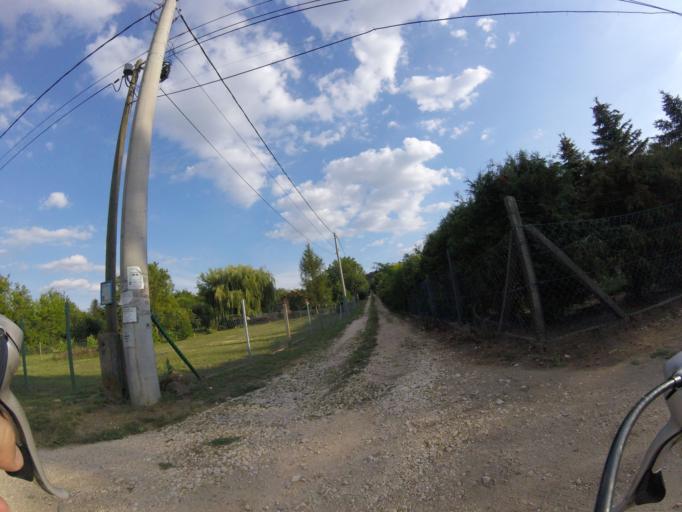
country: HU
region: Pest
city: Budaors
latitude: 47.4403
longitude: 18.9496
